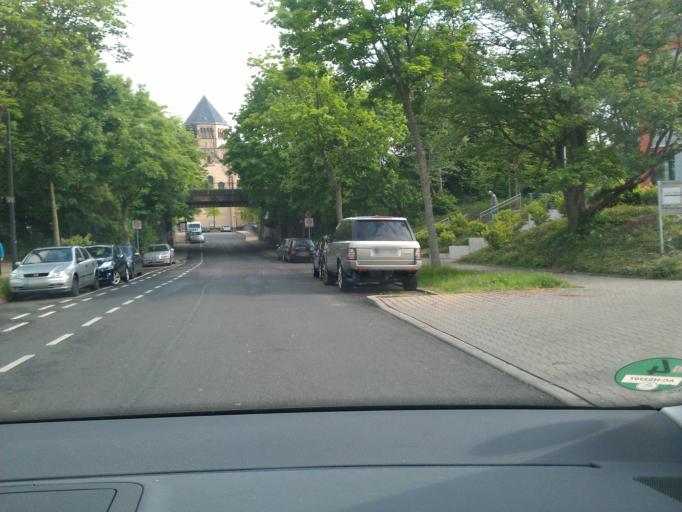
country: DE
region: North Rhine-Westphalia
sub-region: Regierungsbezirk Koln
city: Aachen
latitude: 50.7653
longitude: 6.1094
